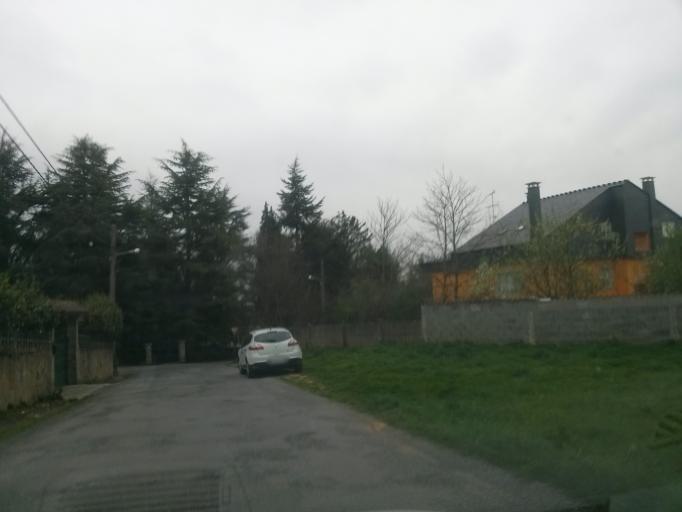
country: ES
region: Galicia
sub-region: Provincia de Lugo
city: Lugo
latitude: 43.0130
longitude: -7.5404
